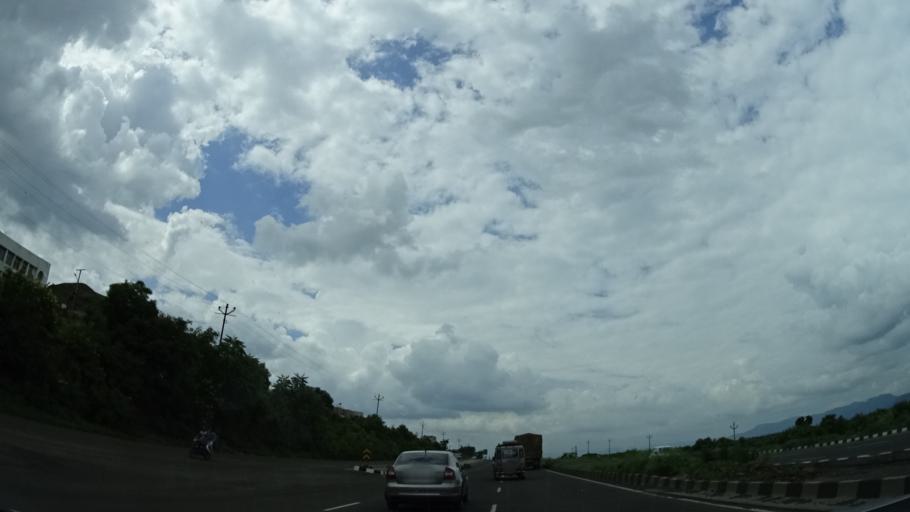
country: IN
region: Maharashtra
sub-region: Satara Division
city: Satara
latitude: 17.7839
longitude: 73.9825
